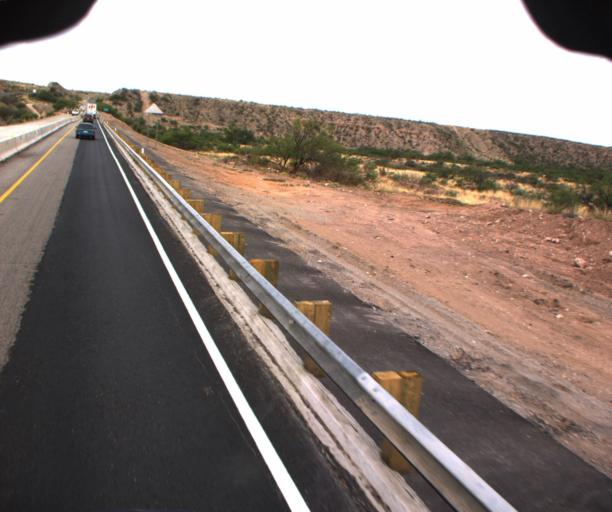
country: US
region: Arizona
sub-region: Pima County
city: Vail
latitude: 31.9980
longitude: -110.6428
